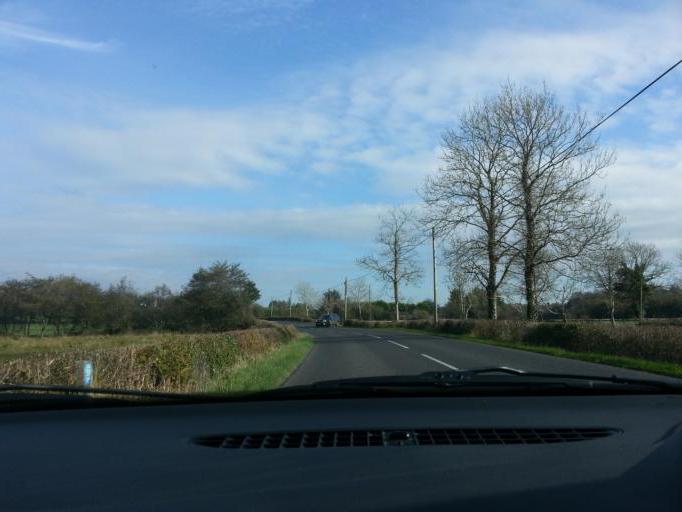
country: IE
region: Ulster
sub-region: County Monaghan
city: Clones
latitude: 54.2247
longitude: -7.3257
